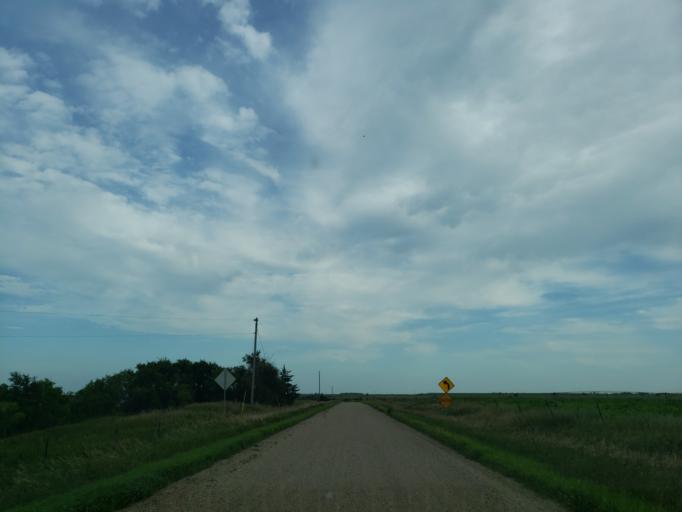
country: US
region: South Dakota
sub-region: Davison County
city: Mitchell
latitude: 43.6867
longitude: -97.9716
